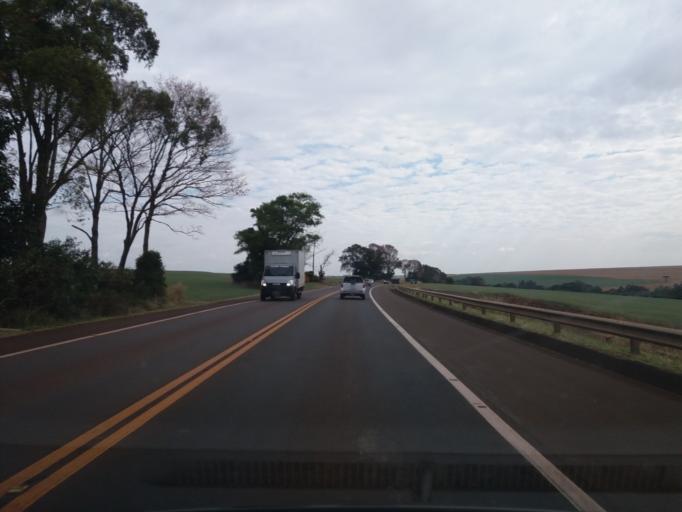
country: BR
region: Parana
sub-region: Campo Mourao
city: Campo Mourao
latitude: -24.3190
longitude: -52.6282
